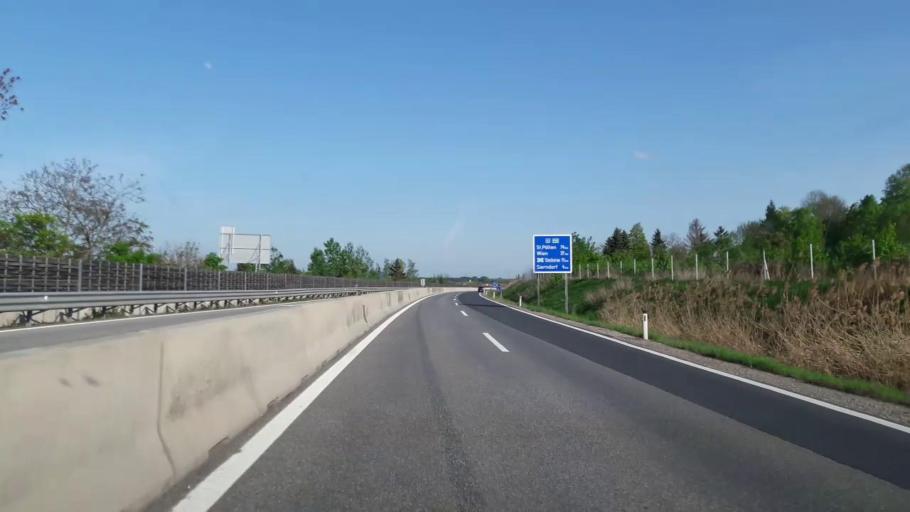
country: AT
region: Lower Austria
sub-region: Politischer Bezirk Hollabrunn
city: Gollersdorf
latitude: 48.4613
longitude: 16.1527
